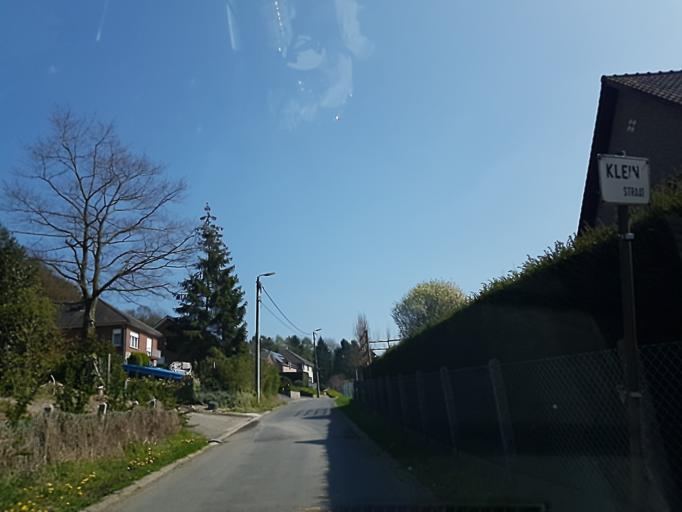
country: BE
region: Flanders
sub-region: Provincie Vlaams-Brabant
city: Oud-Heverlee
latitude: 50.7978
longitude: 4.6520
